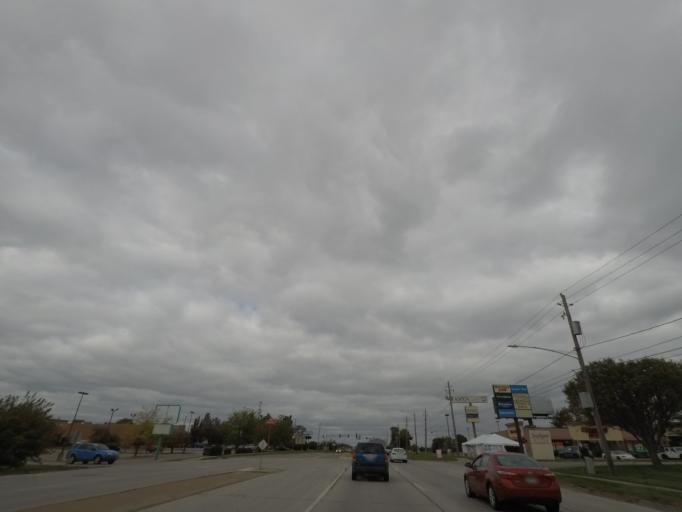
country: US
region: Iowa
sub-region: Polk County
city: Des Moines
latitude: 41.5273
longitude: -93.5967
